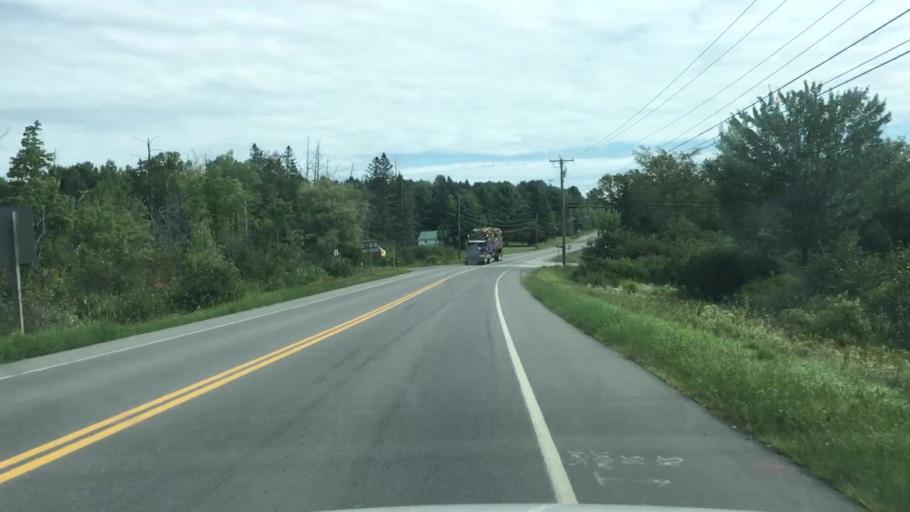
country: US
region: Maine
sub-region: Piscataquis County
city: Dover-Foxcroft
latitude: 45.1973
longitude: -69.2093
